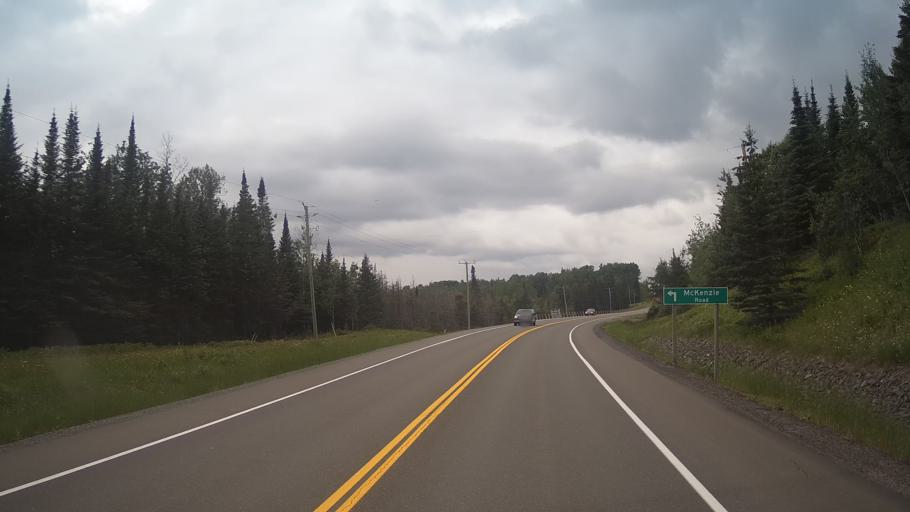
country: CA
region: Ontario
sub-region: Thunder Bay District
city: Thunder Bay
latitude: 48.5109
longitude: -89.4744
